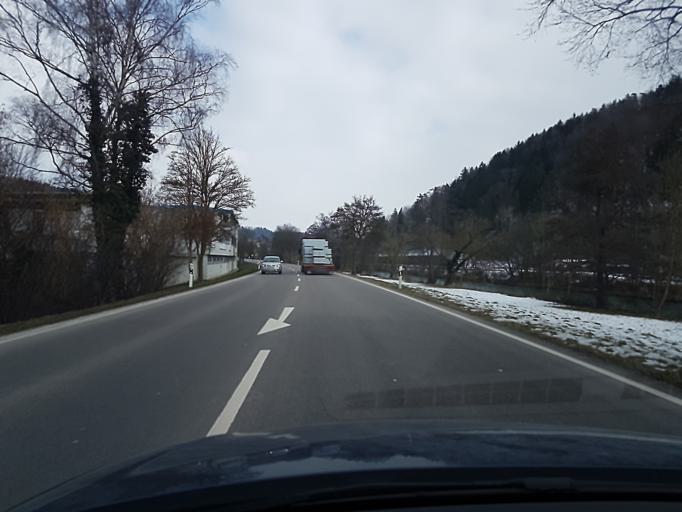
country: DE
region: Baden-Wuerttemberg
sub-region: Karlsruhe Region
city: Horb am Neckar
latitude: 48.4386
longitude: 8.6787
